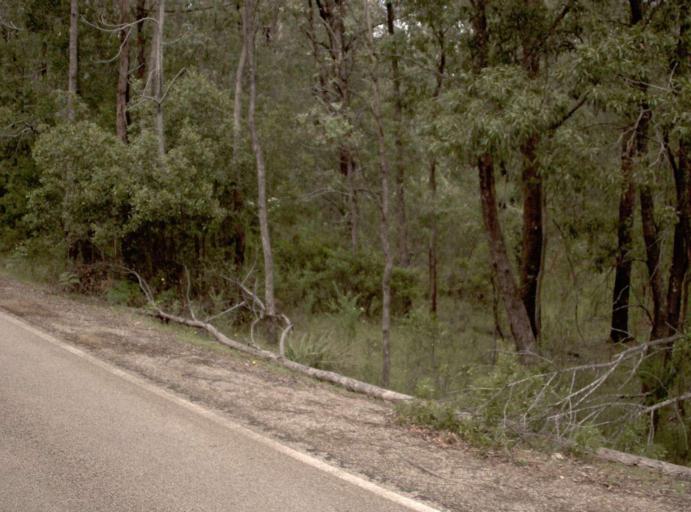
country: AU
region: Victoria
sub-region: East Gippsland
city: Bairnsdale
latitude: -37.6259
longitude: 147.2096
